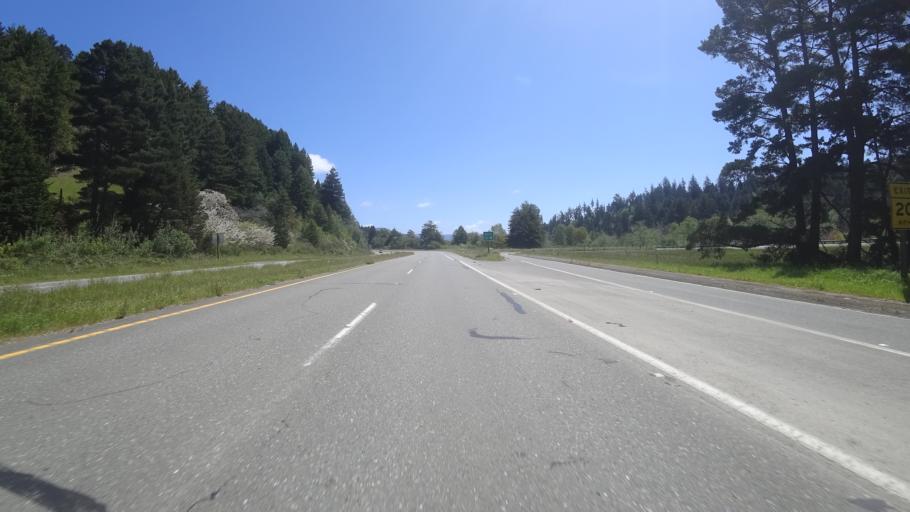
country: US
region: California
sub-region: Humboldt County
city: Arcata
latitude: 40.9098
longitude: -124.0570
